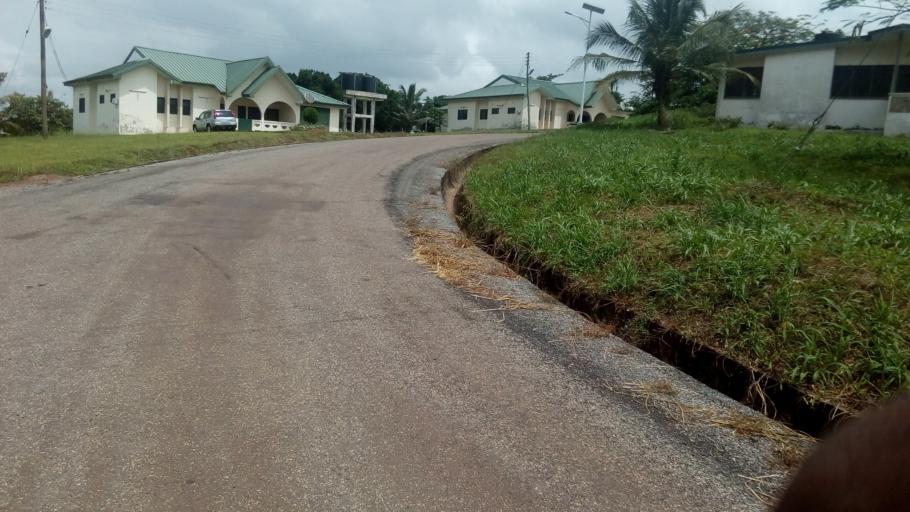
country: GH
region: Western
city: Tarkwa
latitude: 5.2955
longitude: -2.0126
